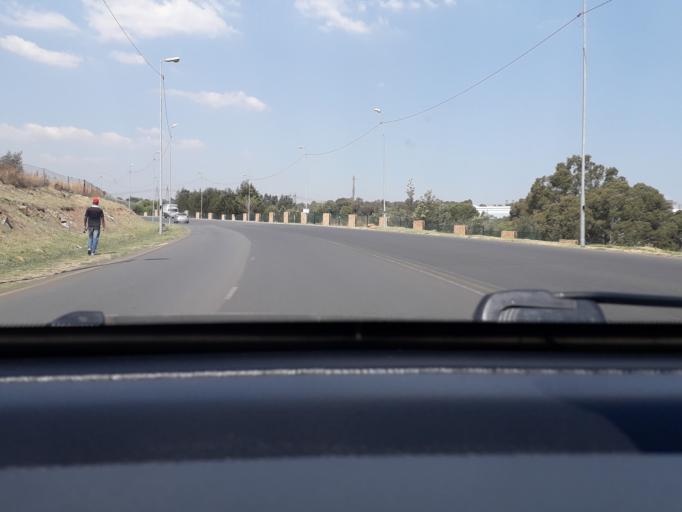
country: ZA
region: Gauteng
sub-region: City of Johannesburg Metropolitan Municipality
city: Modderfontein
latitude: -26.1028
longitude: 28.1674
